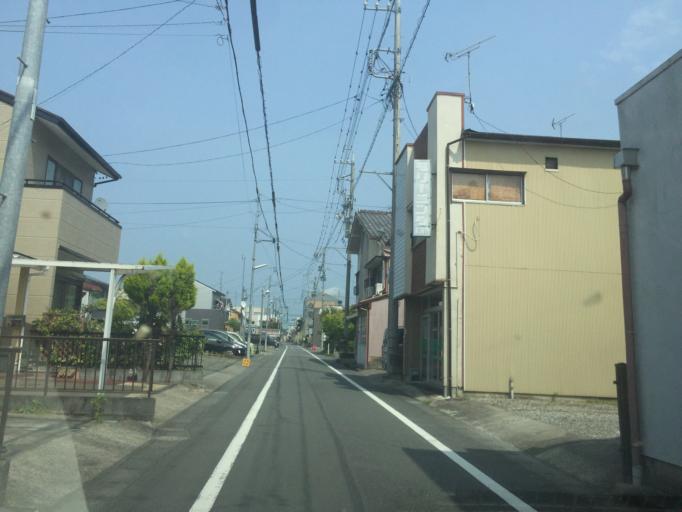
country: JP
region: Shizuoka
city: Kakegawa
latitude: 34.7720
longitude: 138.0118
